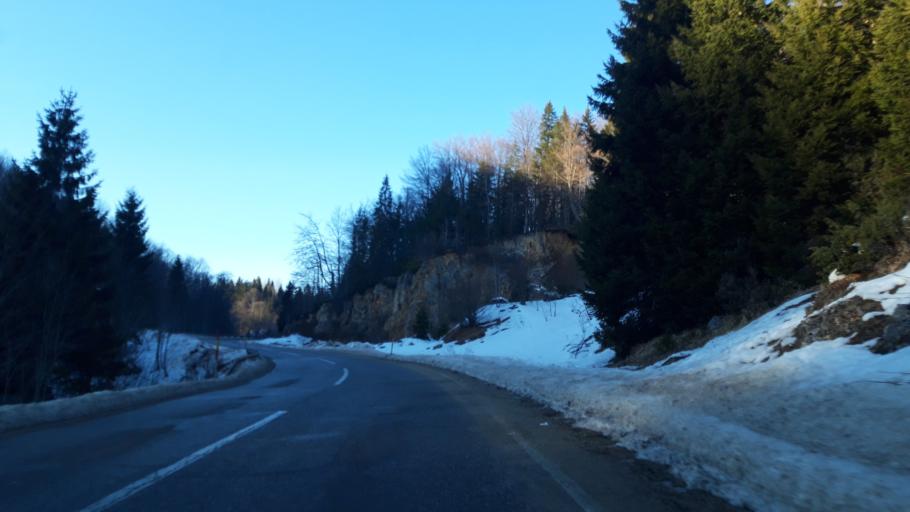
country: BA
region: Republika Srpska
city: Han Pijesak
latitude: 44.1285
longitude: 18.9607
